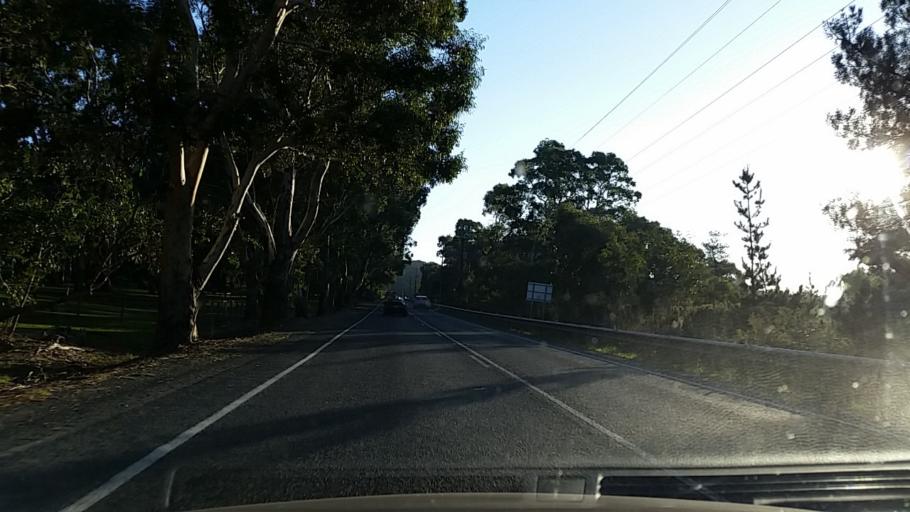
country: AU
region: South Australia
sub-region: Alexandrina
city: Mount Compass
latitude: -35.3434
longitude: 138.6116
